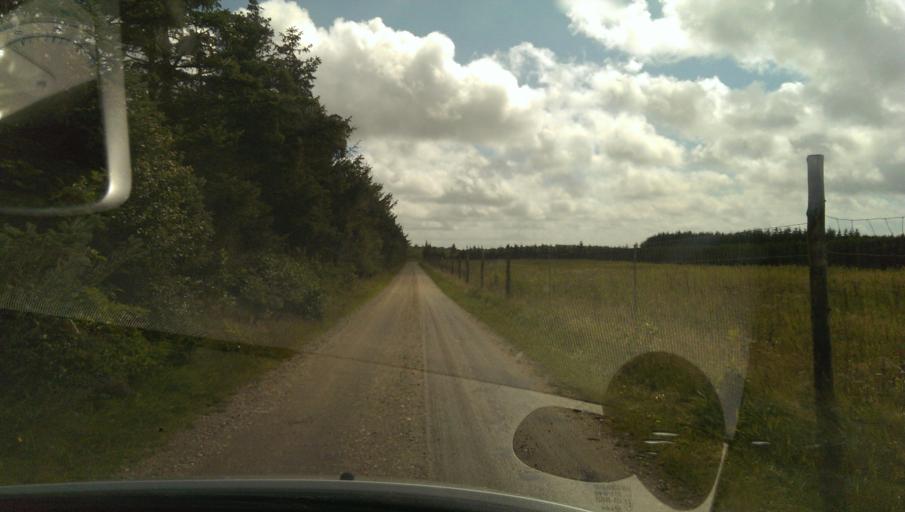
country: DK
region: South Denmark
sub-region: Varde Kommune
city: Varde
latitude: 55.6058
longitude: 8.4508
